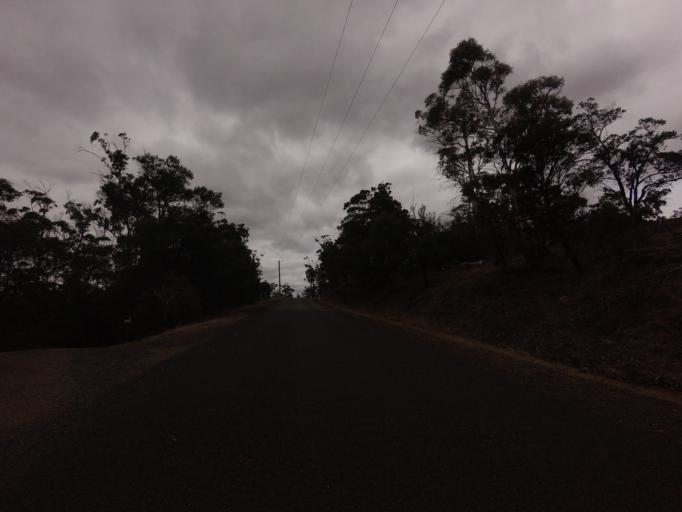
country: AU
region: Tasmania
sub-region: Clarence
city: Cambridge
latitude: -42.7918
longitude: 147.4018
